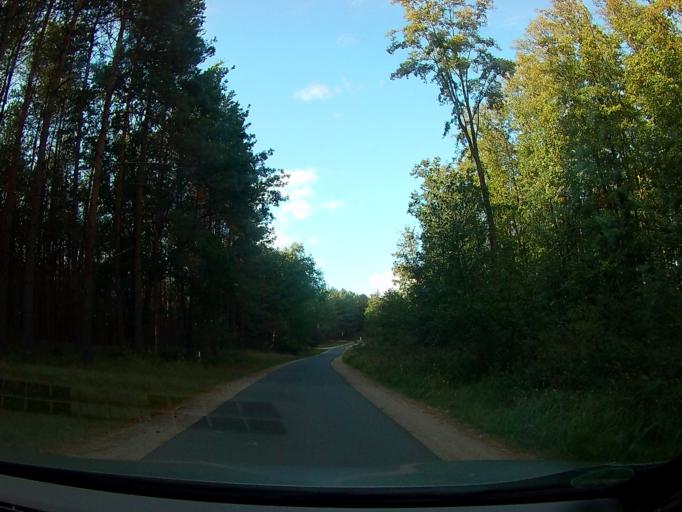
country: DE
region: Mecklenburg-Vorpommern
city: Wesenberg
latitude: 53.2965
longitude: 12.9352
